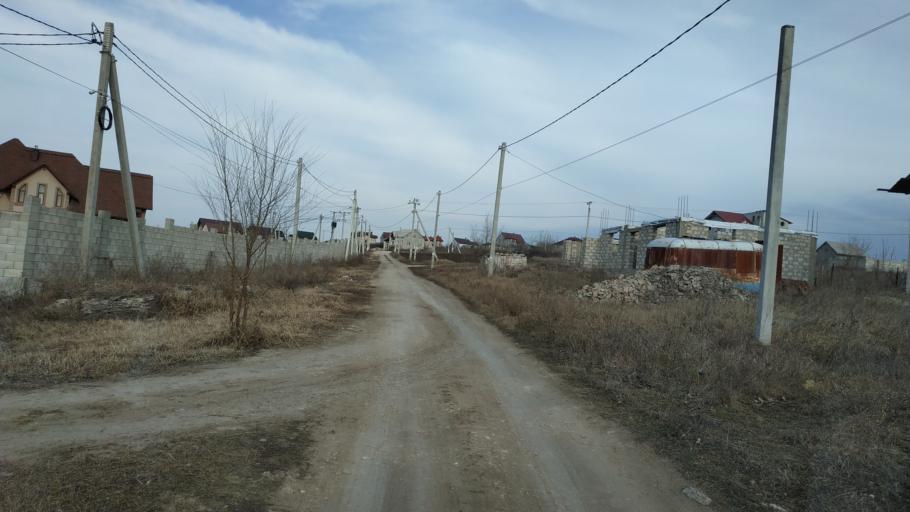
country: MD
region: Chisinau
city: Vatra
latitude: 46.9913
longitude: 28.6666
